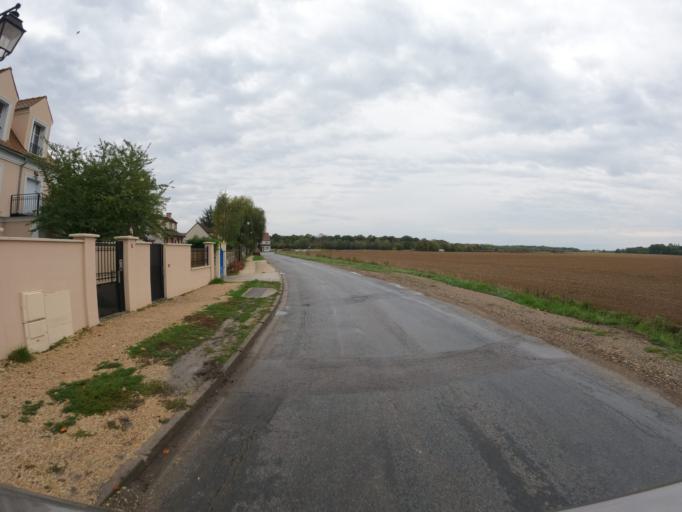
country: FR
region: Ile-de-France
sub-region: Departement de Seine-et-Marne
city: Serris
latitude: 48.8168
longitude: 2.7918
